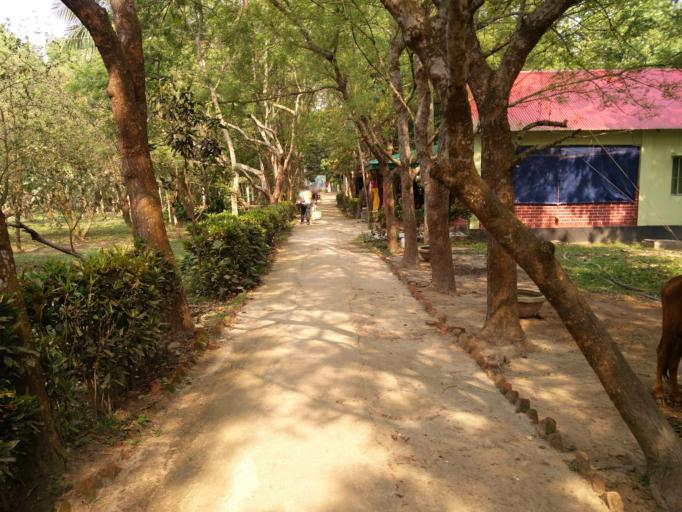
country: BD
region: Dhaka
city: Sherpur
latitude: 24.9173
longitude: 90.1582
